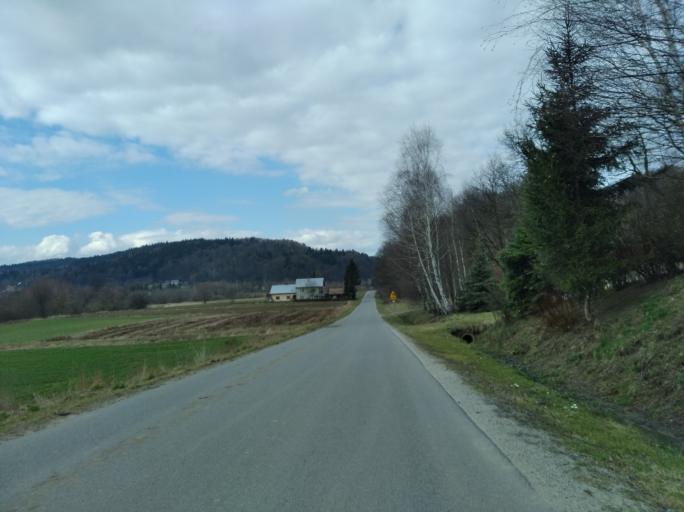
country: PL
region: Subcarpathian Voivodeship
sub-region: Powiat strzyzowski
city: Frysztak
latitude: 49.8470
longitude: 21.6266
